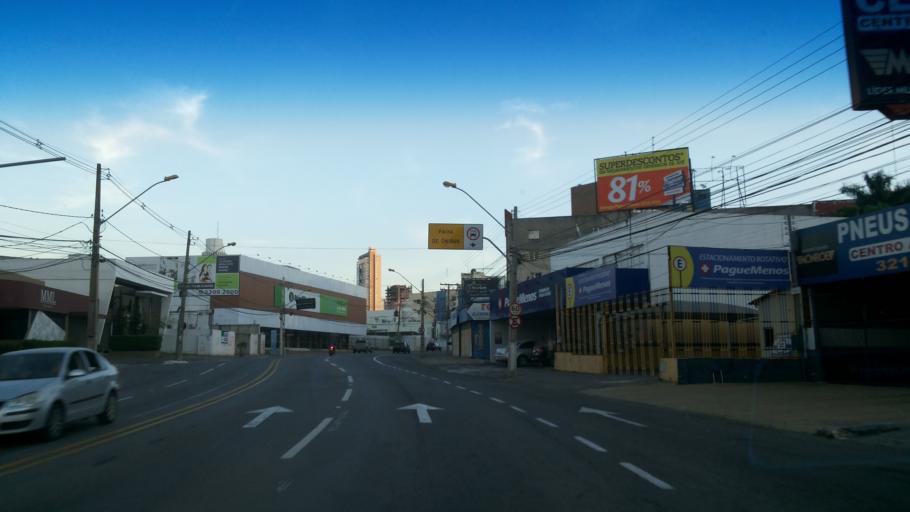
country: BR
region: Goias
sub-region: Goiania
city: Goiania
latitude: -16.6868
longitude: -49.2597
